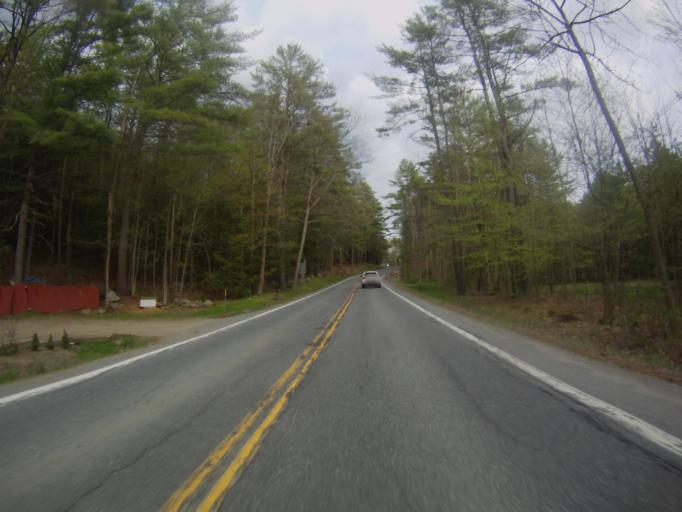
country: US
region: New York
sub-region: Warren County
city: Warrensburg
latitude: 43.6708
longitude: -73.7651
